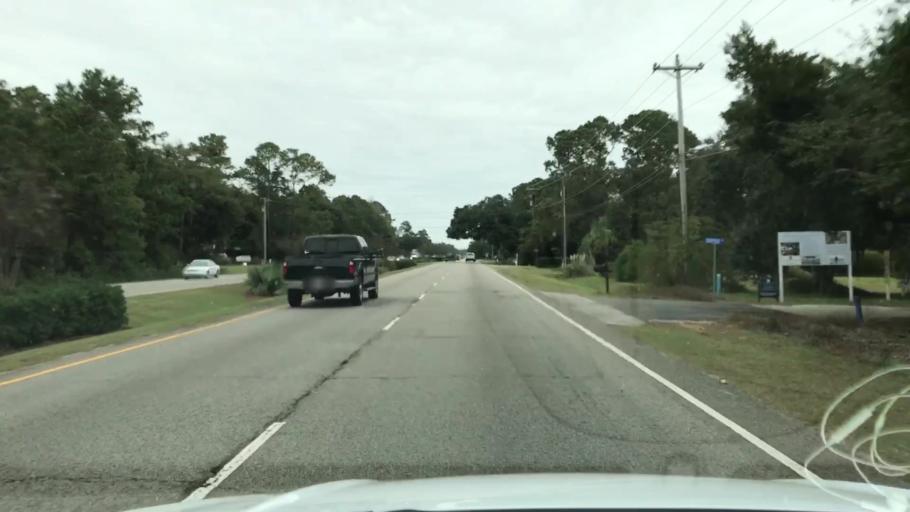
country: US
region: South Carolina
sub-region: Georgetown County
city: Murrells Inlet
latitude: 33.4624
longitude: -79.1107
